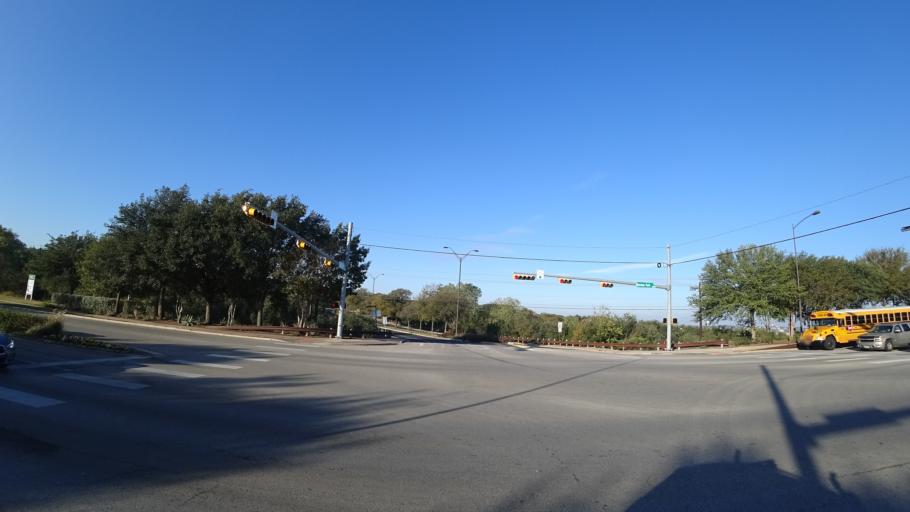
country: US
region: Texas
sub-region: Travis County
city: Hudson Bend
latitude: 30.3775
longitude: -97.8847
